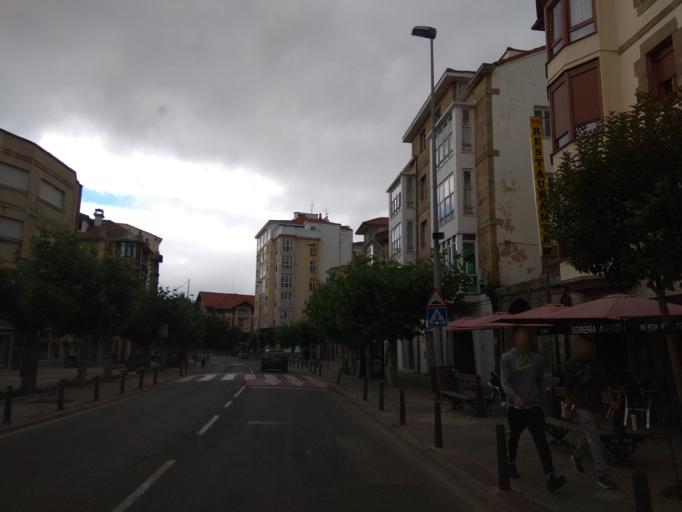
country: ES
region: Cantabria
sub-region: Provincia de Cantabria
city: Reinosa
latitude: 42.9984
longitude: -4.1387
